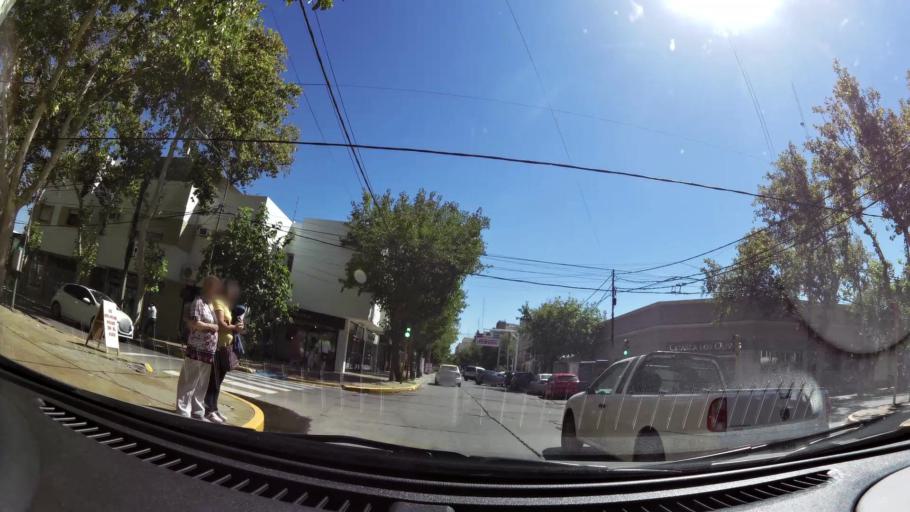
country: AR
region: San Juan
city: San Juan
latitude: -31.5415
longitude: -68.5240
